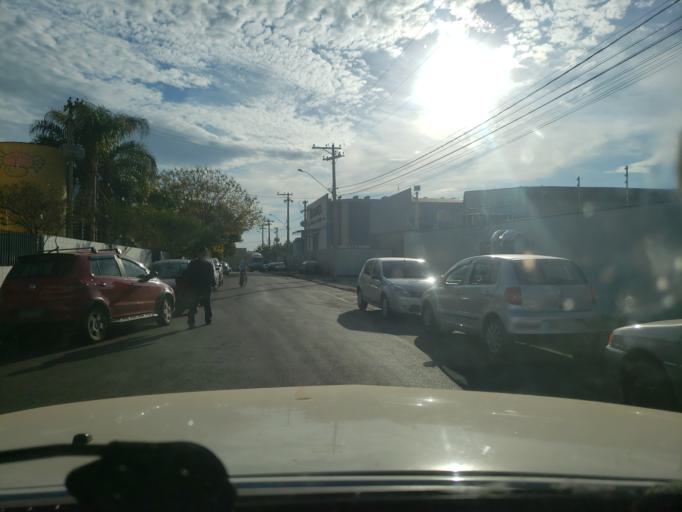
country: BR
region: Sao Paulo
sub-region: Moji-Guacu
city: Mogi-Gaucu
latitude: -22.3244
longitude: -46.9284
